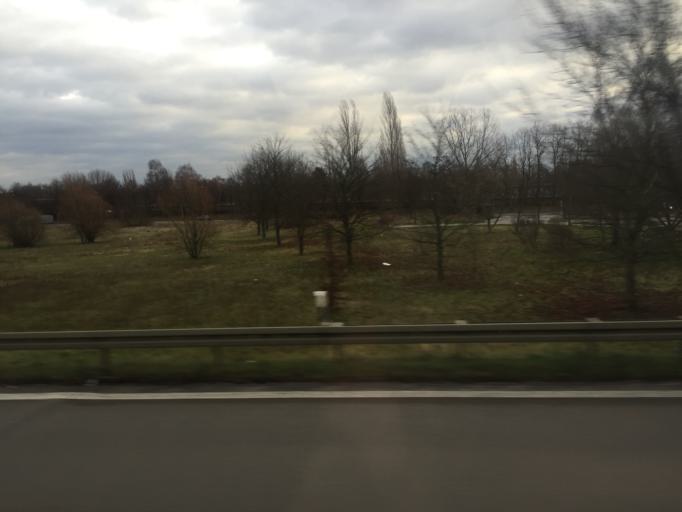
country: DE
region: Berlin
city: Heinersdorf
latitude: 52.5810
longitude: 13.4296
